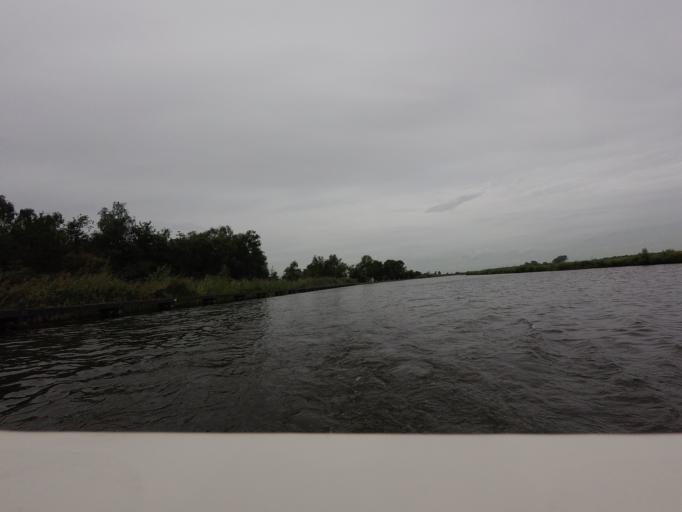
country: NL
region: Friesland
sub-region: Gemeente Boarnsterhim
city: Warten
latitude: 53.1147
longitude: 5.8874
